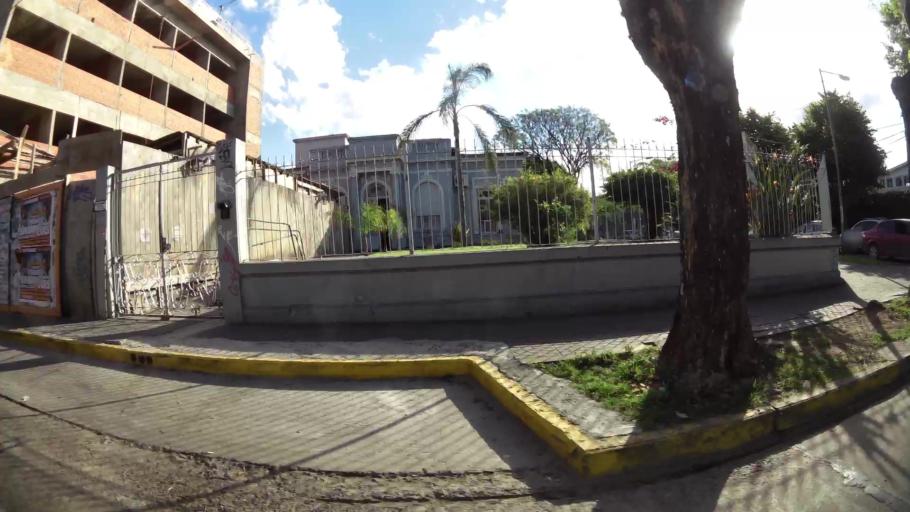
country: AR
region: Buenos Aires
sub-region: Partido de General San Martin
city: General San Martin
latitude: -34.5474
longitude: -58.5587
